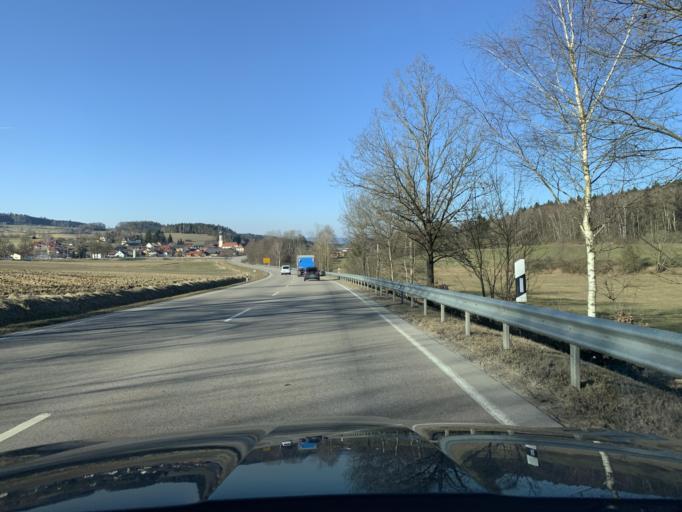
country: DE
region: Bavaria
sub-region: Upper Palatinate
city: Pemfling
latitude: 49.2953
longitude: 12.6295
